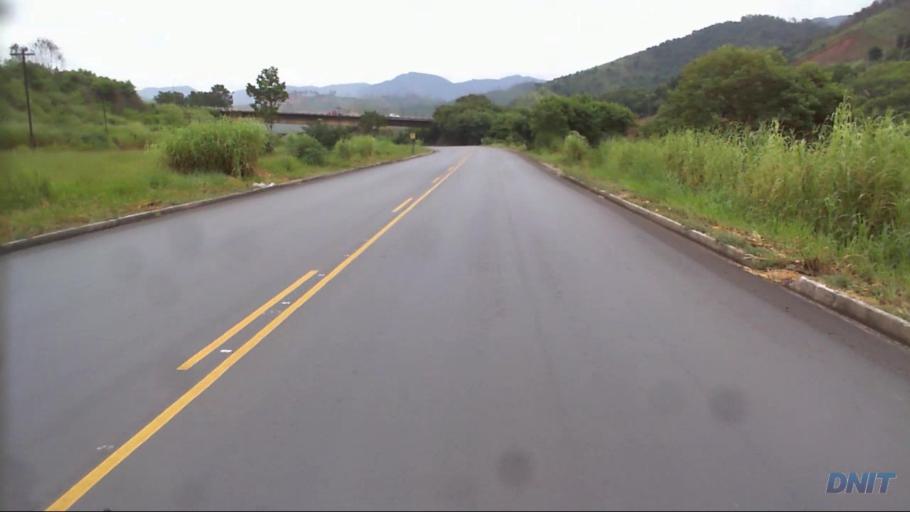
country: BR
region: Minas Gerais
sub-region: Coronel Fabriciano
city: Coronel Fabriciano
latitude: -19.5260
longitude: -42.6379
